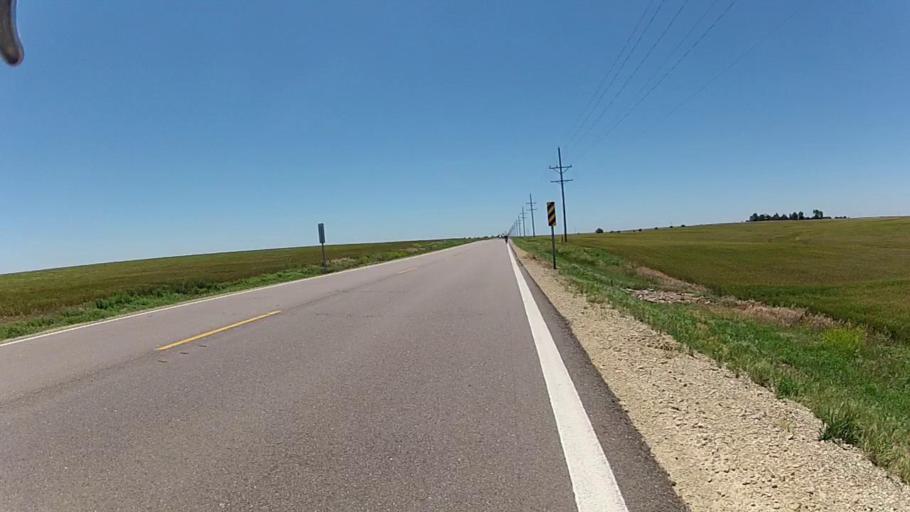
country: US
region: Kansas
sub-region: Kiowa County
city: Greensburg
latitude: 37.5318
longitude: -99.3207
